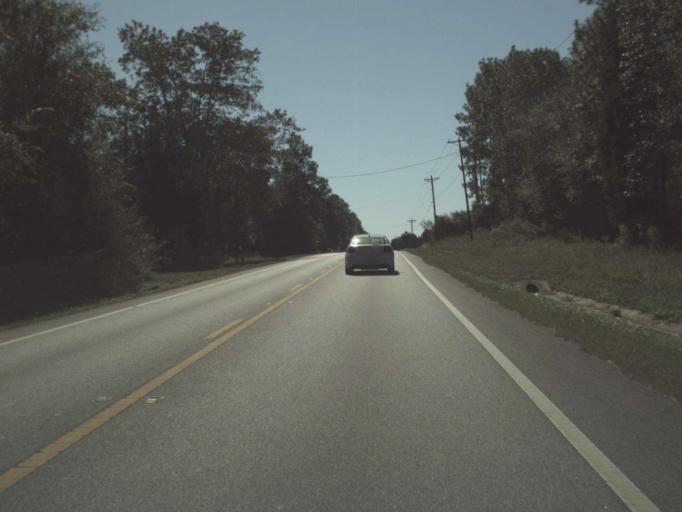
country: US
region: Florida
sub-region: Walton County
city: DeFuniak Springs
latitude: 30.8021
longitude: -86.1230
